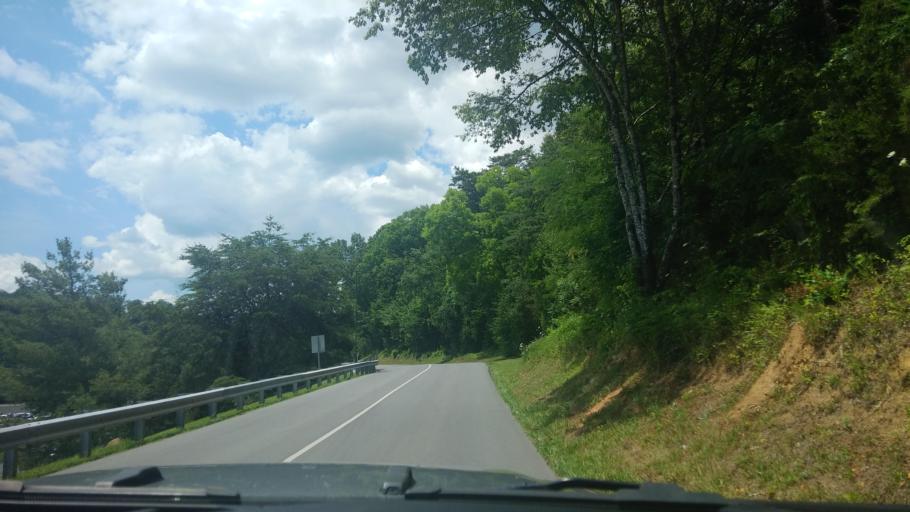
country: US
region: Tennessee
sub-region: Sevier County
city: Pigeon Forge
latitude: 35.8035
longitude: -83.5359
